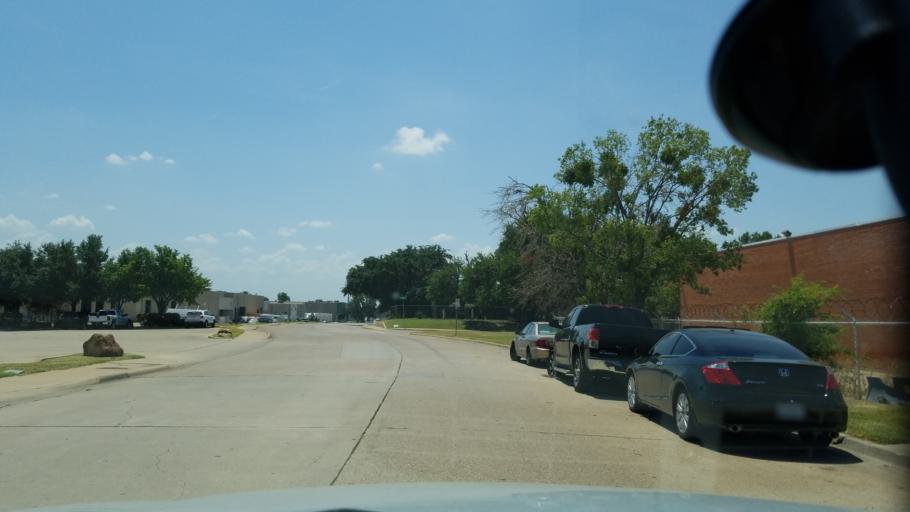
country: US
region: Texas
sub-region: Dallas County
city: Farmers Branch
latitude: 32.8915
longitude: -96.8831
